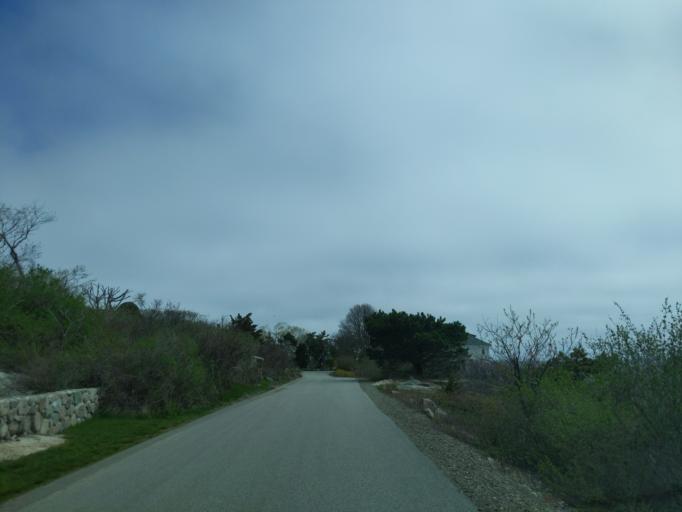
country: US
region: Massachusetts
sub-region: Essex County
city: Rockport
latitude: 42.6439
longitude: -70.5959
